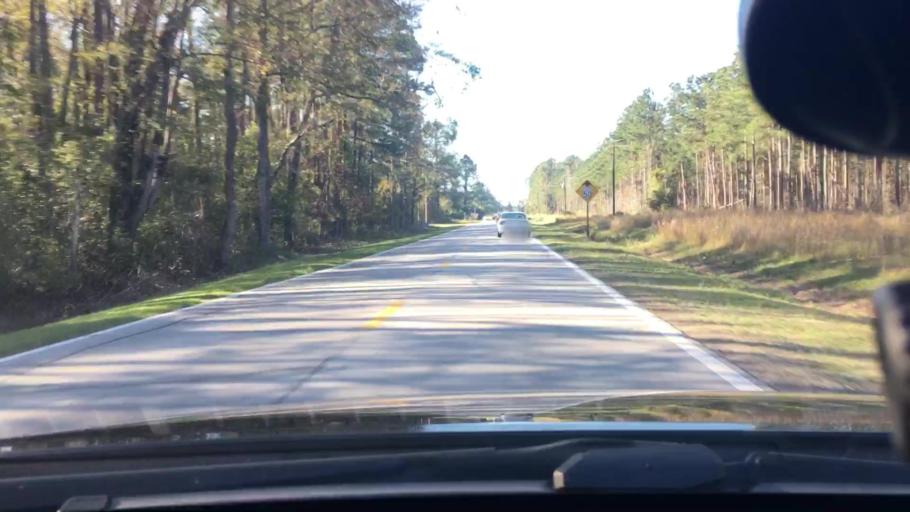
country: US
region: North Carolina
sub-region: Craven County
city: Vanceboro
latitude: 35.2255
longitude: -77.1311
